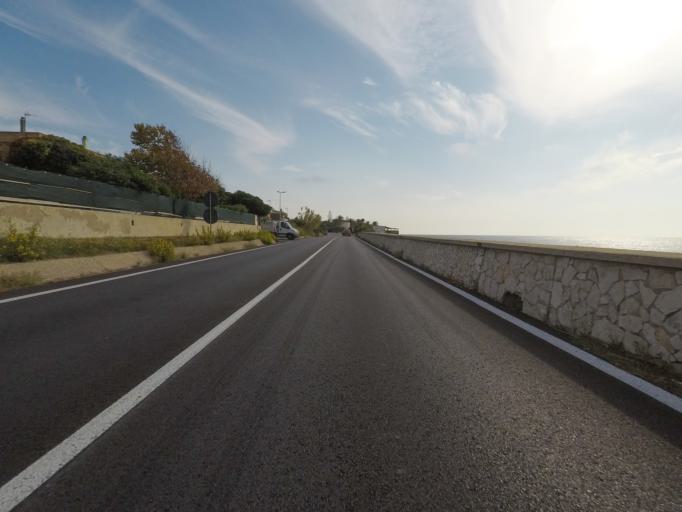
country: IT
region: Latium
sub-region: Citta metropolitana di Roma Capitale
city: Civitavecchia
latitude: 42.0518
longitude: 11.8203
